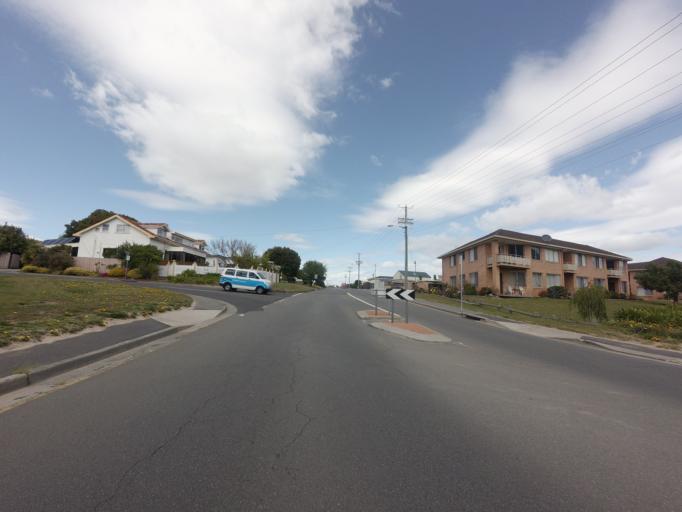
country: AU
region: Tasmania
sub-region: Clarence
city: Howrah
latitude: -42.8840
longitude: 147.4056
